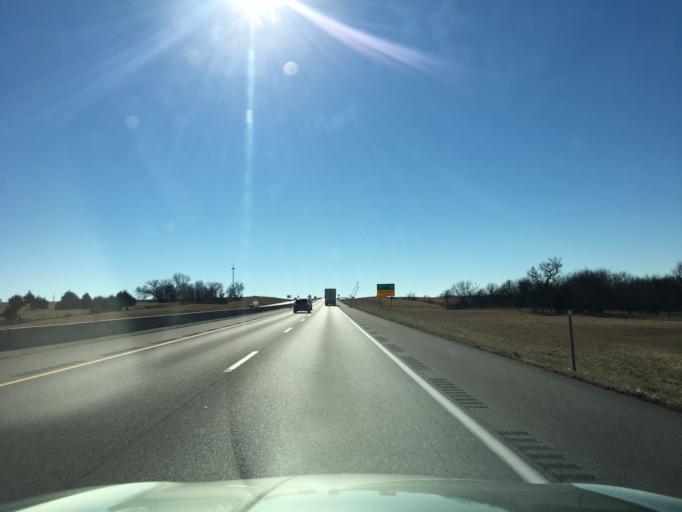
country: US
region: Kansas
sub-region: Sumner County
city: Wellington
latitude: 37.2564
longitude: -97.3390
